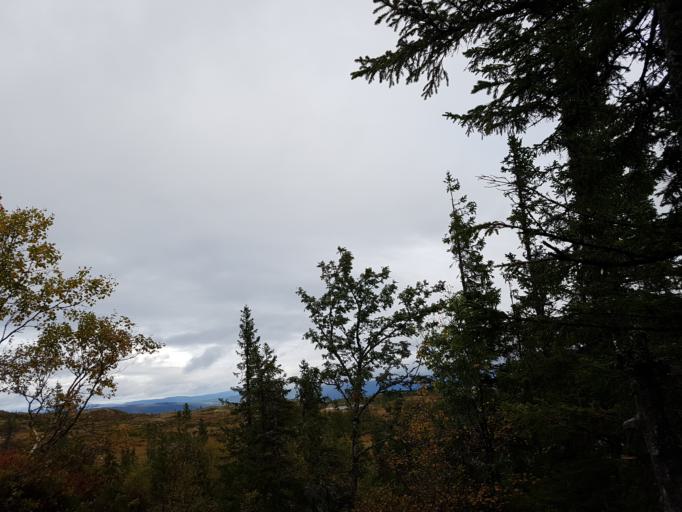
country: NO
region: Sor-Trondelag
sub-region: Melhus
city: Melhus
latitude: 63.4055
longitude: 10.2052
